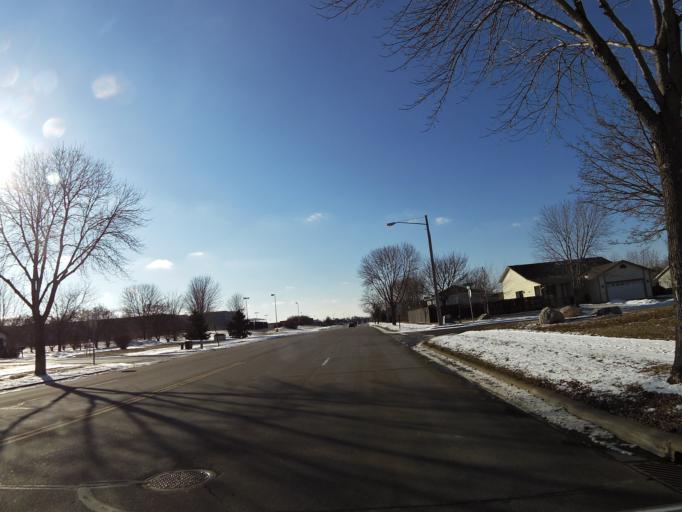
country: US
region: Minnesota
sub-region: Scott County
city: Shakopee
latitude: 44.7809
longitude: -93.4991
